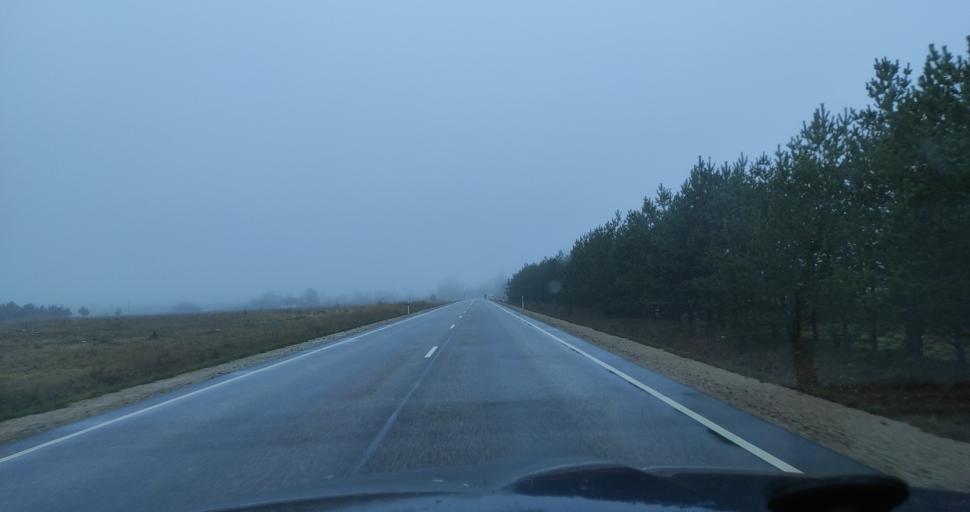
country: LV
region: Pavilostas
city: Pavilosta
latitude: 56.9403
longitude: 21.2820
